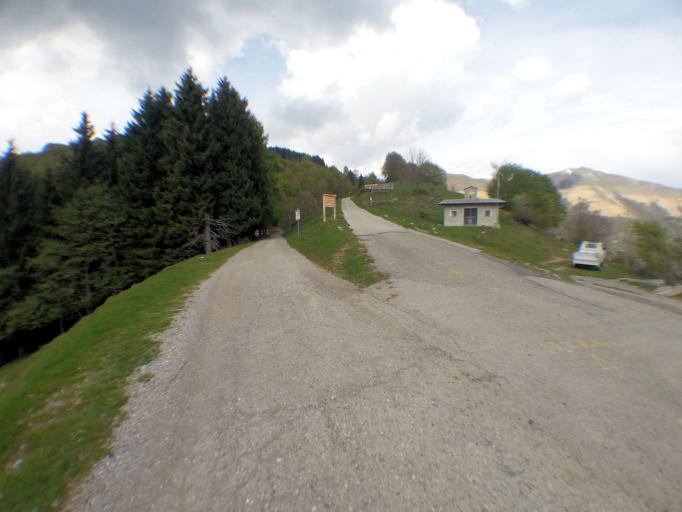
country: IT
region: Lombardy
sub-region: Provincia di Como
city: Sala Comacina
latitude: 45.9896
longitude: 9.1505
